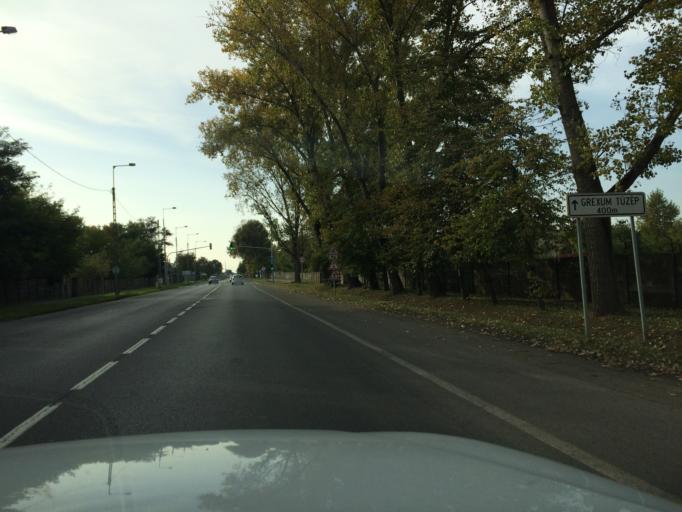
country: HU
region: Szabolcs-Szatmar-Bereg
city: Nyiregyhaza
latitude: 47.9570
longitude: 21.6800
